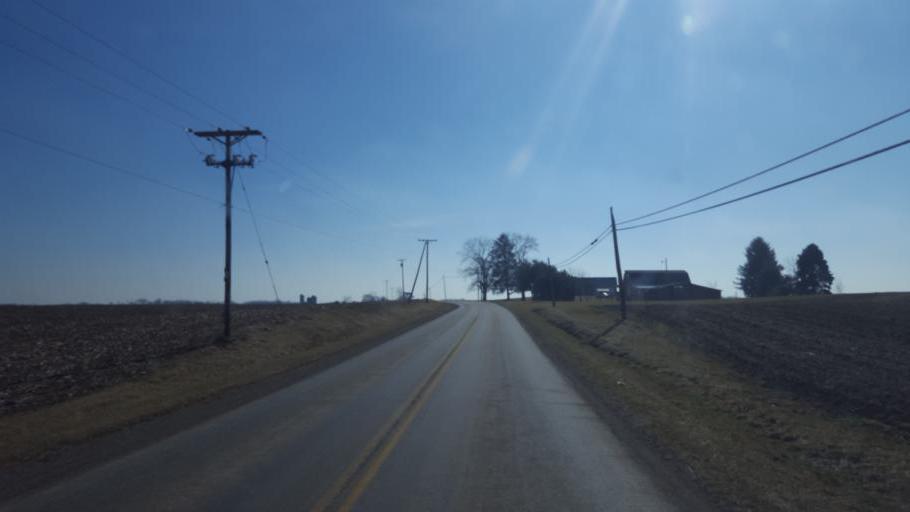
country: US
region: Ohio
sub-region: Richland County
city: Shelby
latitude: 40.9220
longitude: -82.5777
